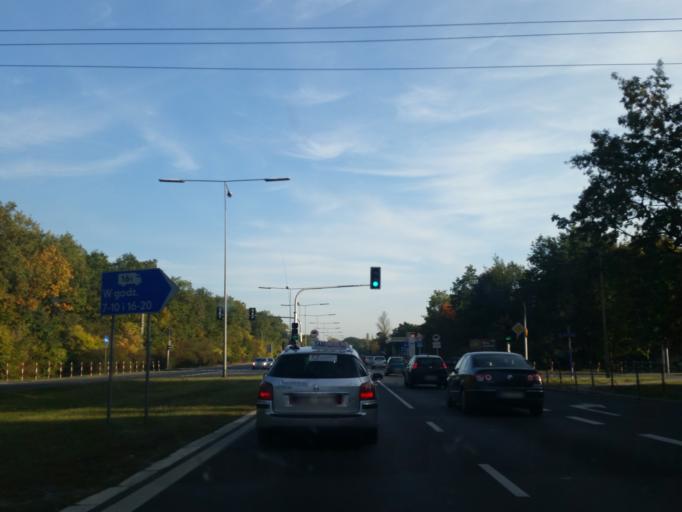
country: PL
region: Masovian Voivodeship
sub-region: Warszawa
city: Bielany
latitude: 52.3148
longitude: 20.9205
